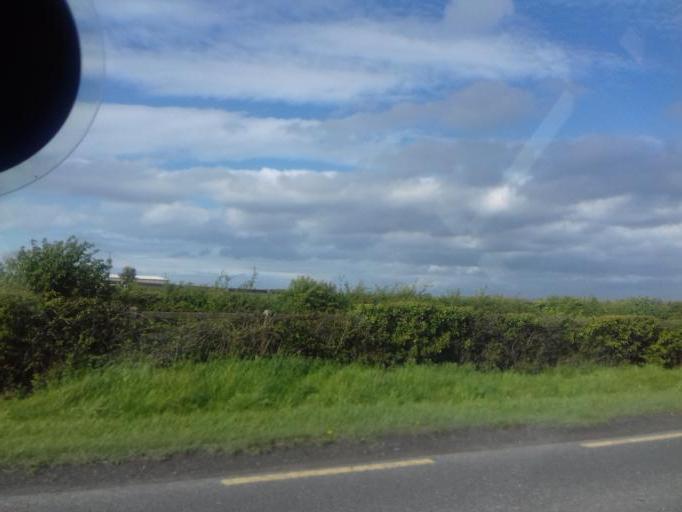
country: IE
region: Leinster
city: Ballymun
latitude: 53.4392
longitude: -6.2840
